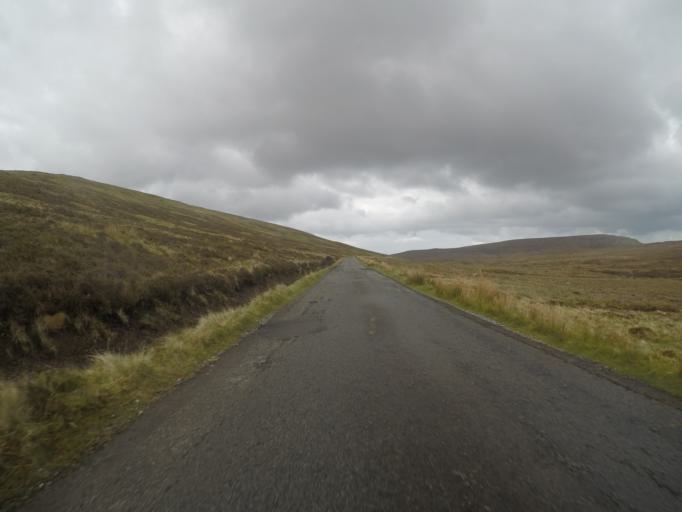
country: GB
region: Scotland
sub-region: Highland
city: Portree
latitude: 57.6232
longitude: -6.3048
